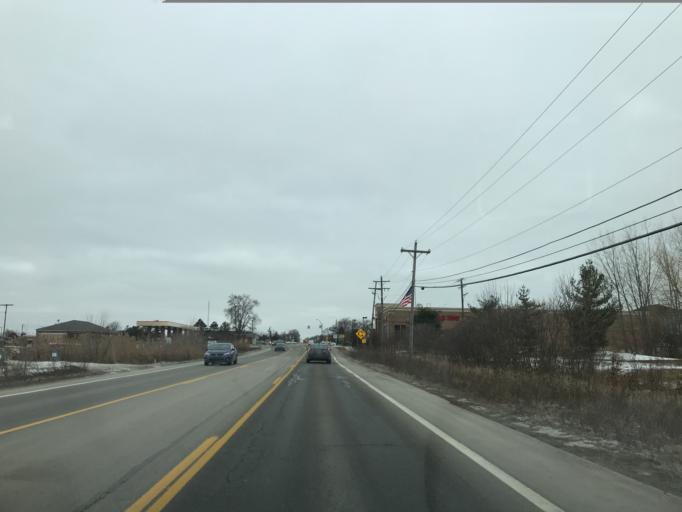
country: US
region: Michigan
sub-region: Washtenaw County
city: Ann Arbor
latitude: 42.2295
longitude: -83.7356
